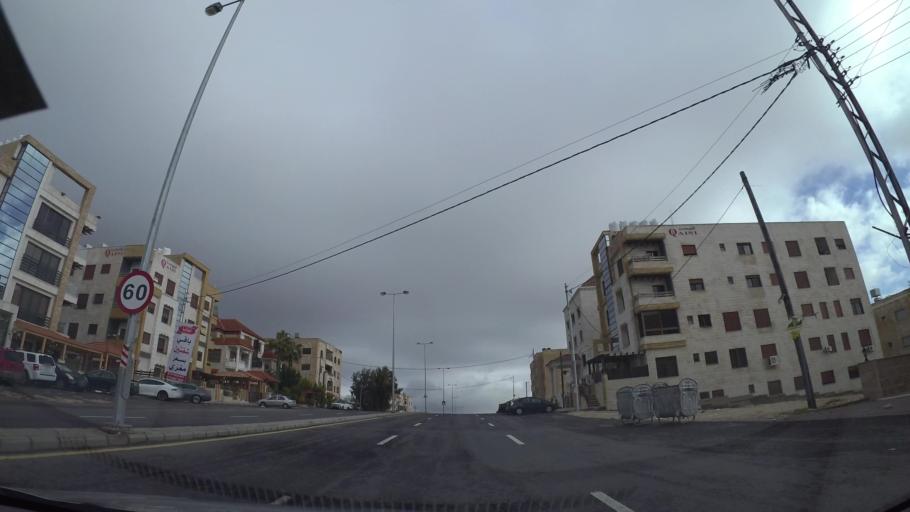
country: JO
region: Amman
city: Al Jubayhah
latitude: 32.0325
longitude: 35.8828
